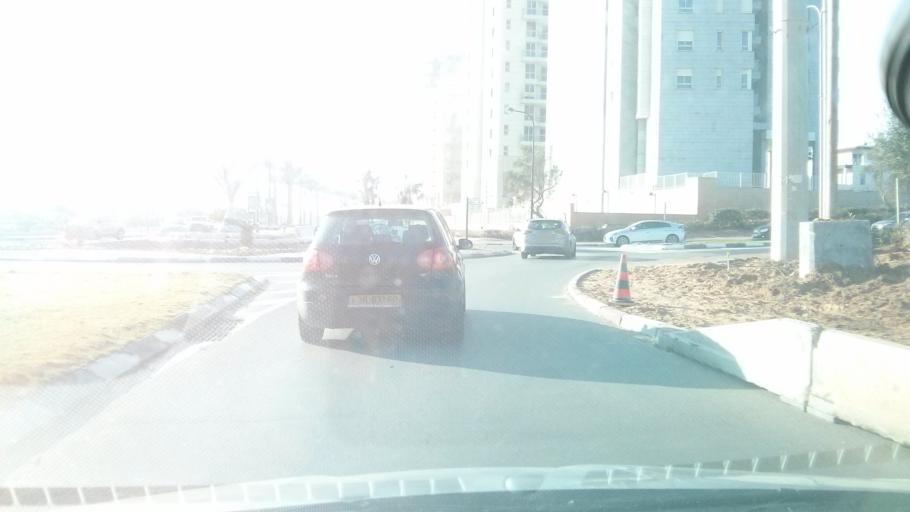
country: IL
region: Central District
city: Netanya
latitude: 32.3171
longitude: 34.8477
